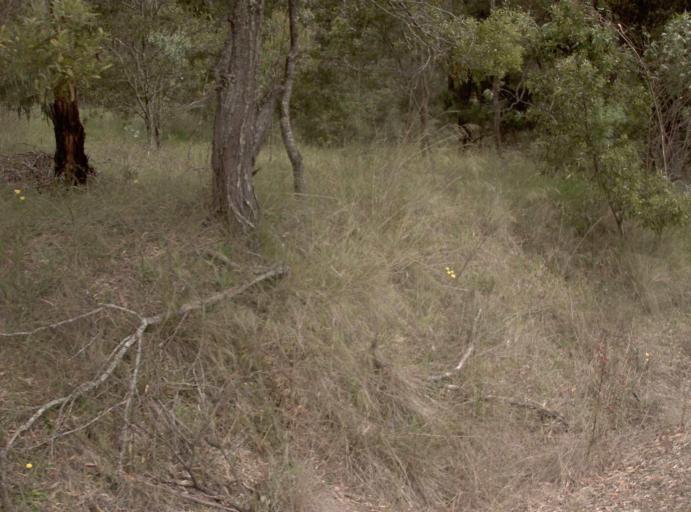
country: AU
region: Victoria
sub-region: East Gippsland
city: Bairnsdale
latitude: -37.5813
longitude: 147.1816
